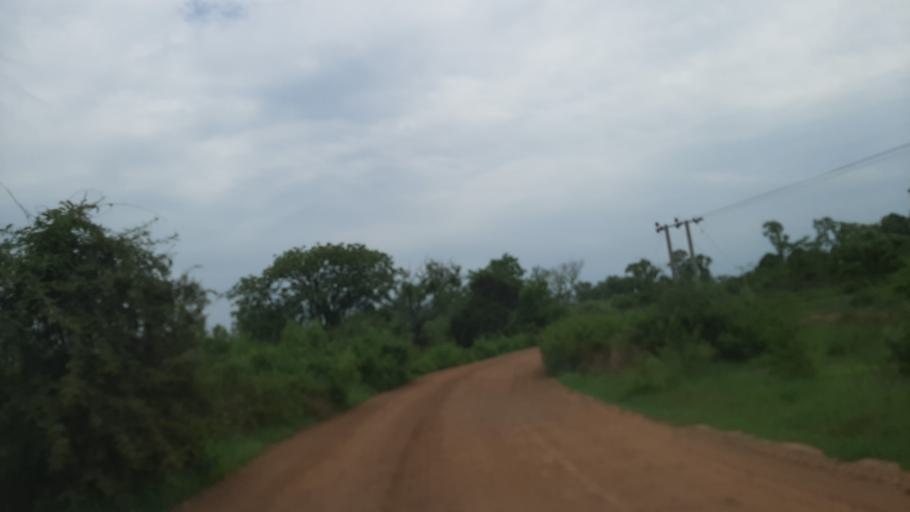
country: ET
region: Gambela
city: Gambela
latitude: 8.2188
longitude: 34.5642
